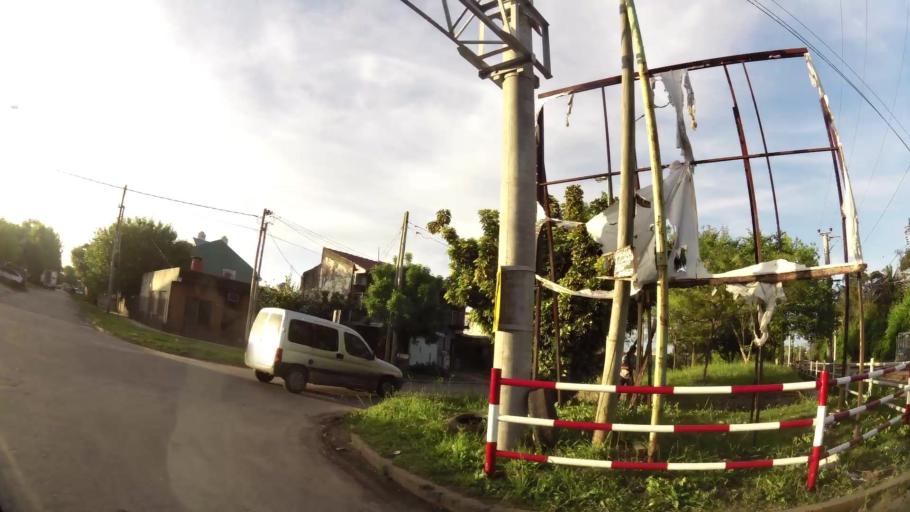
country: AR
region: Buenos Aires
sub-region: Partido de Quilmes
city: Quilmes
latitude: -34.7792
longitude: -58.1977
